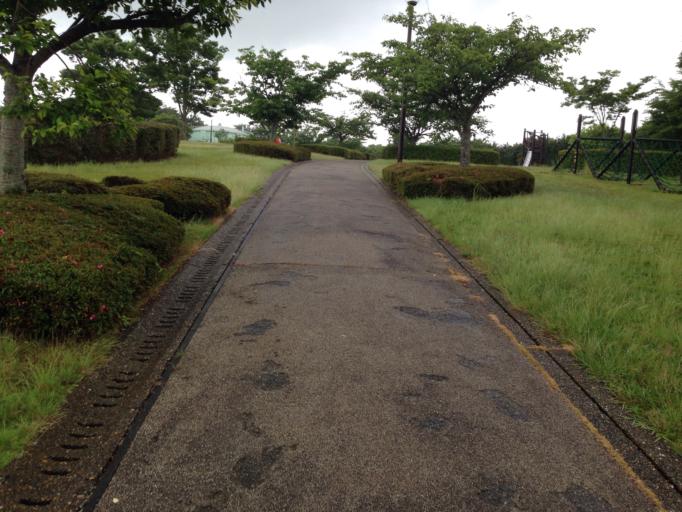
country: JP
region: Shizuoka
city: Fukuroi
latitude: 34.7446
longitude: 137.9414
